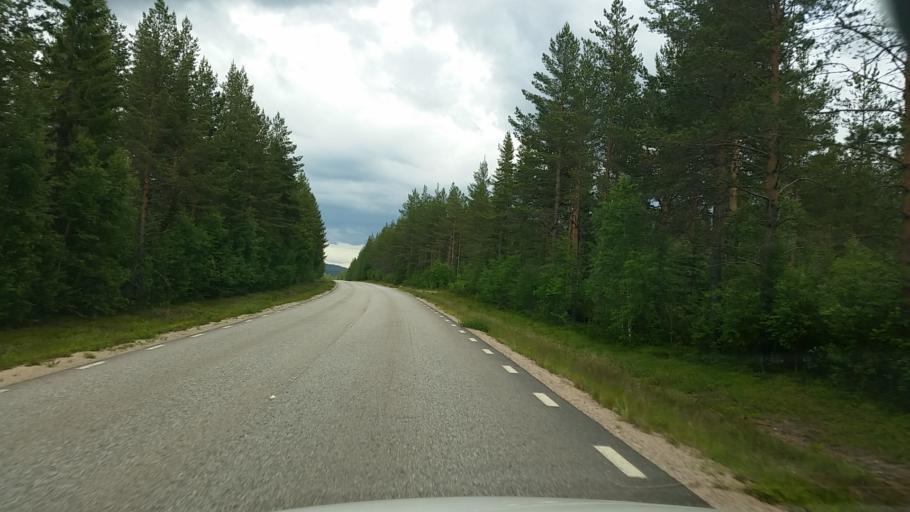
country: SE
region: Jaemtland
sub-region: Harjedalens Kommun
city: Sveg
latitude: 61.9799
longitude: 15.0860
